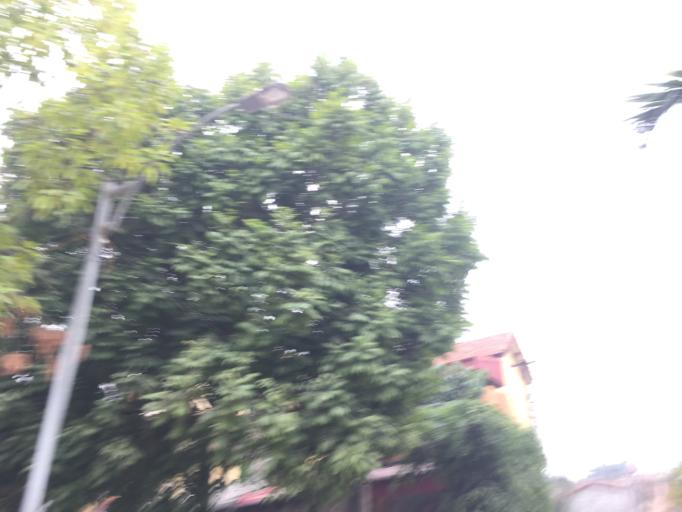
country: VN
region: Hung Yen
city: Van Giang
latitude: 20.9699
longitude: 105.9201
